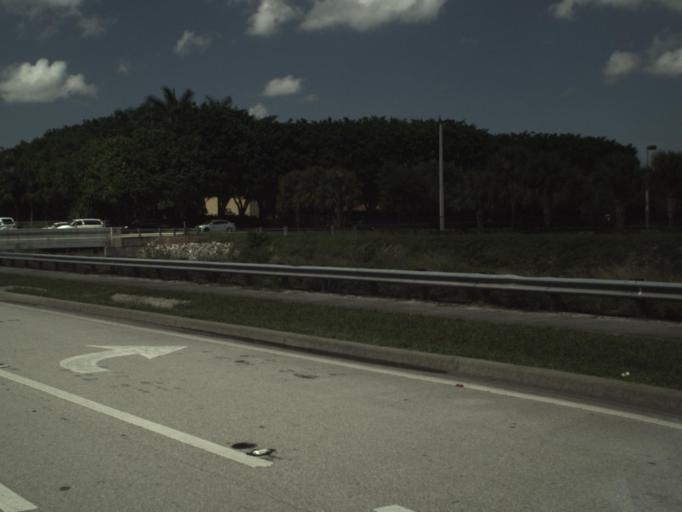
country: US
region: Florida
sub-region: Palm Beach County
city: Wellington
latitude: 26.6351
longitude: -80.2040
